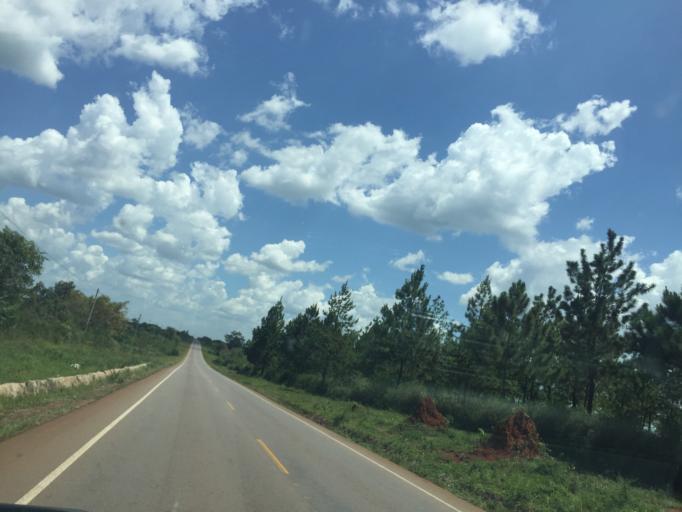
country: UG
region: Central Region
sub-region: Nakasongola District
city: Nakasongola
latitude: 1.3727
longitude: 32.3504
